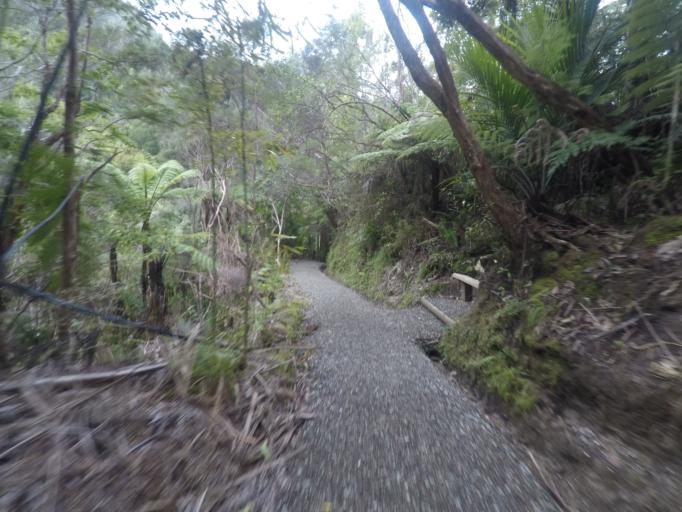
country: NZ
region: Auckland
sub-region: Auckland
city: Titirangi
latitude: -37.0009
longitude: 174.5523
